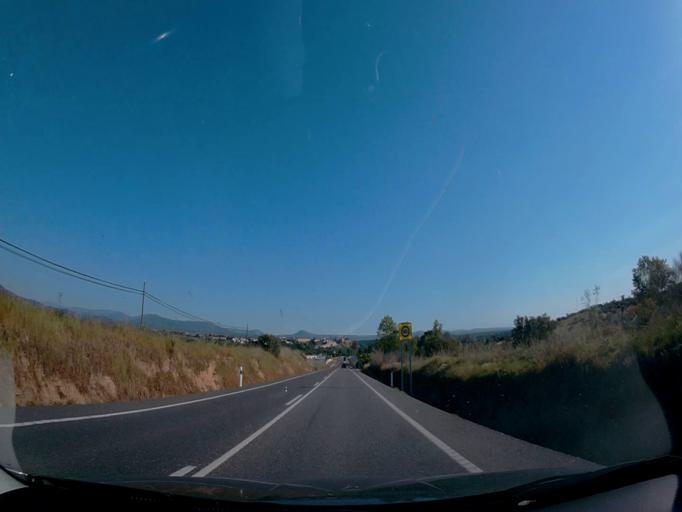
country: ES
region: Castille-La Mancha
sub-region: Province of Toledo
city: Escalona
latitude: 40.1493
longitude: -4.4028
